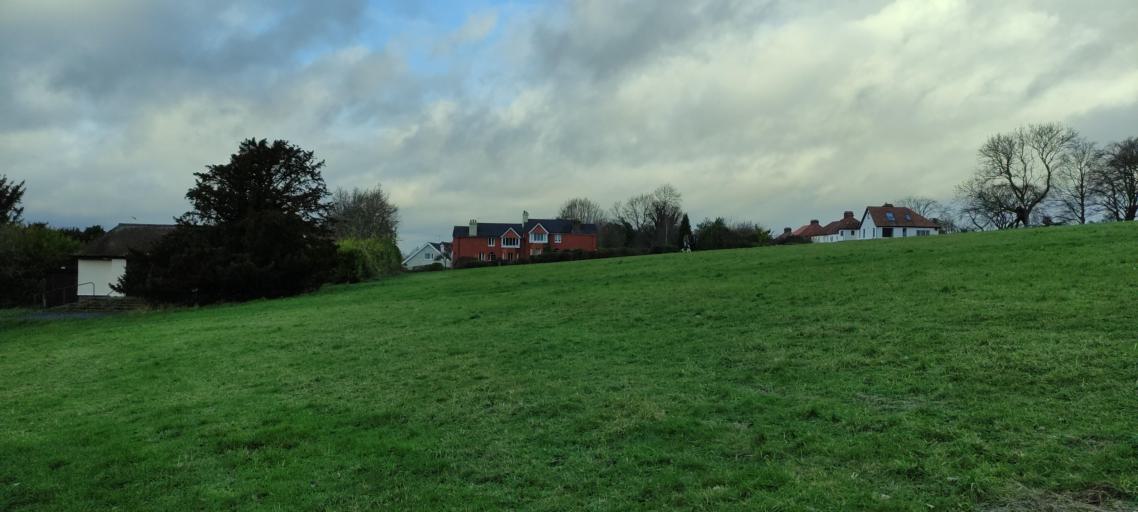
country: GB
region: England
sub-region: Greater London
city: Purley
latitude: 51.3281
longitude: -0.1011
